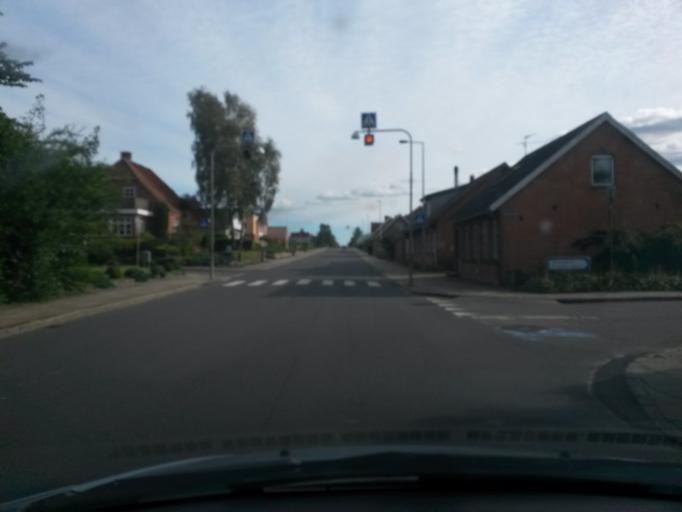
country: DK
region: Central Jutland
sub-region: Silkeborg Kommune
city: Kjellerup
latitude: 56.2849
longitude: 9.4322
